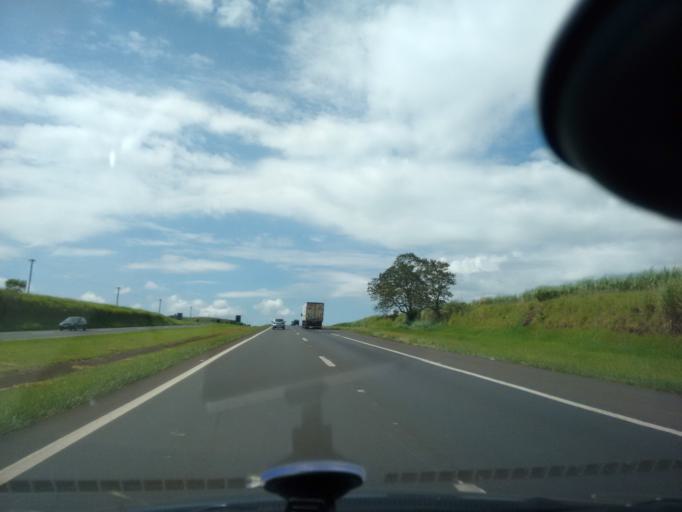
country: BR
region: Sao Paulo
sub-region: Ibate
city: Ibate
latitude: -21.8848
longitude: -48.0841
